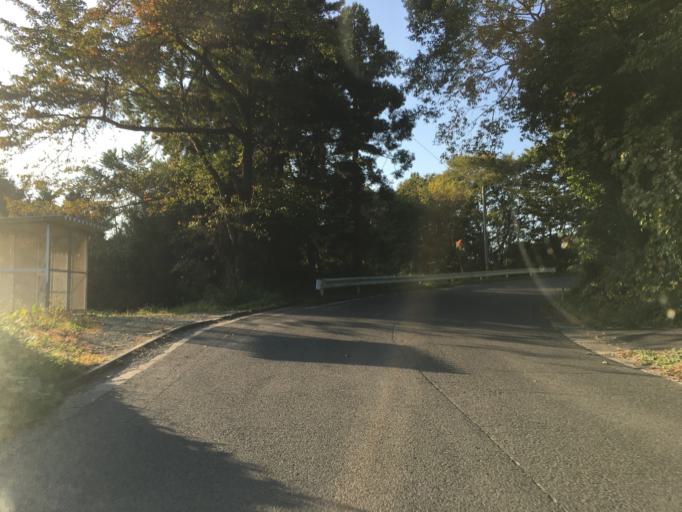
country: JP
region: Fukushima
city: Fukushima-shi
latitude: 37.6416
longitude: 140.5729
